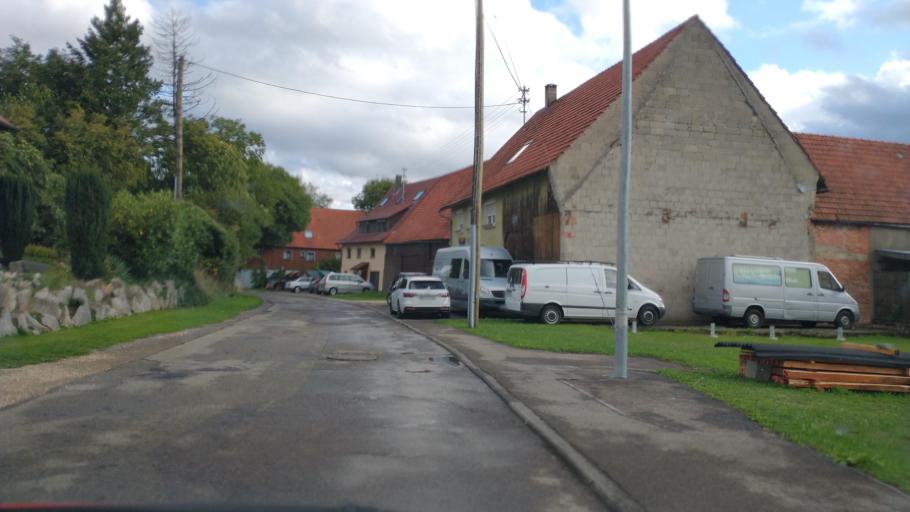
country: DE
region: Baden-Wuerttemberg
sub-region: Regierungsbezirk Stuttgart
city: Alfdorf
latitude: 48.8564
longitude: 9.6919
